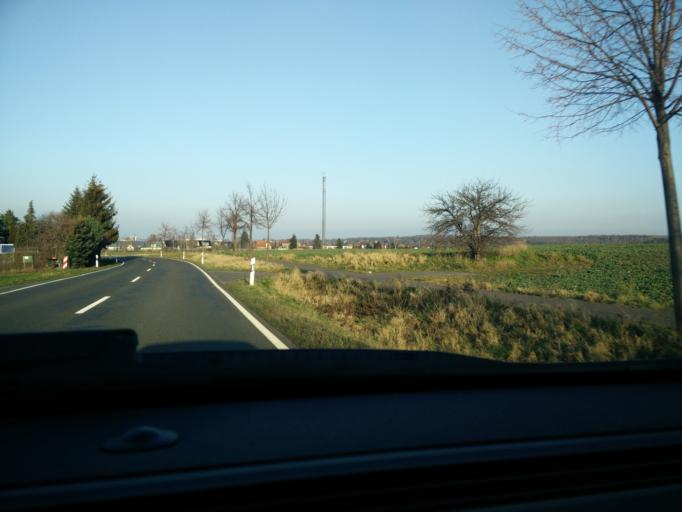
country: DE
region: Saxony
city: Grossbardau
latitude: 51.1997
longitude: 12.7002
